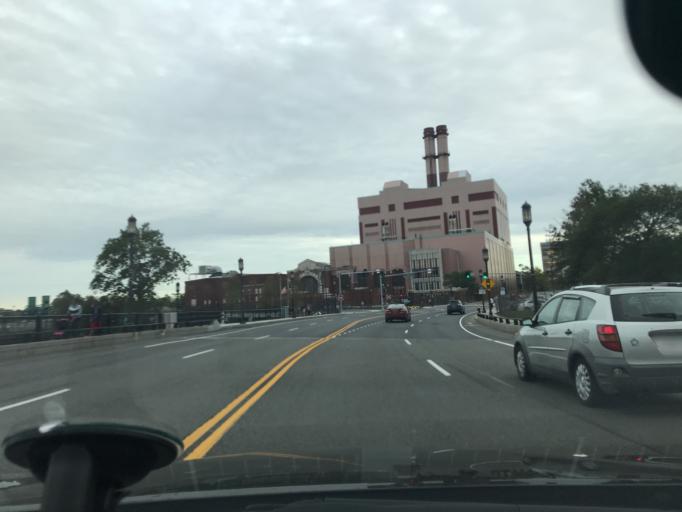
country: US
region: Massachusetts
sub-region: Suffolk County
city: South Boston
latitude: 42.3420
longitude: -71.0359
